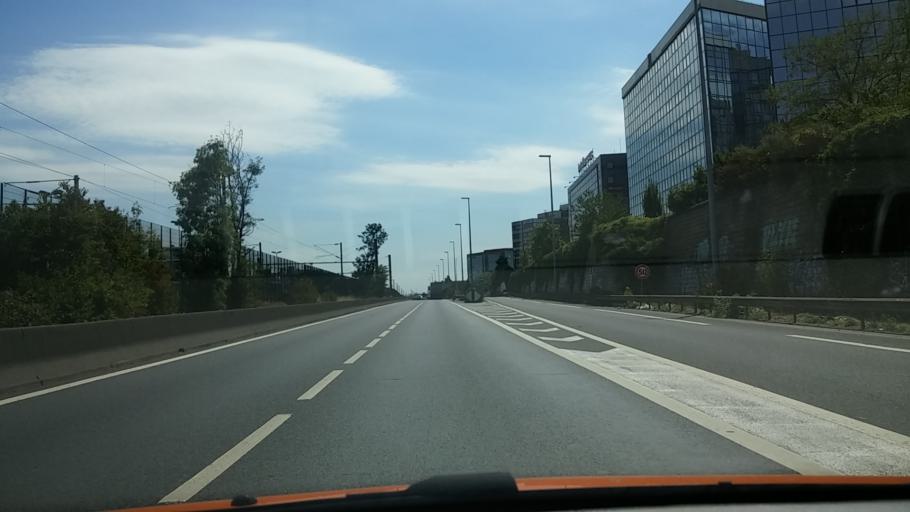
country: FR
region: Ile-de-France
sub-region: Departement du Val-de-Marne
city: Fontenay-sous-Bois
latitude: 48.8560
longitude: 2.4881
